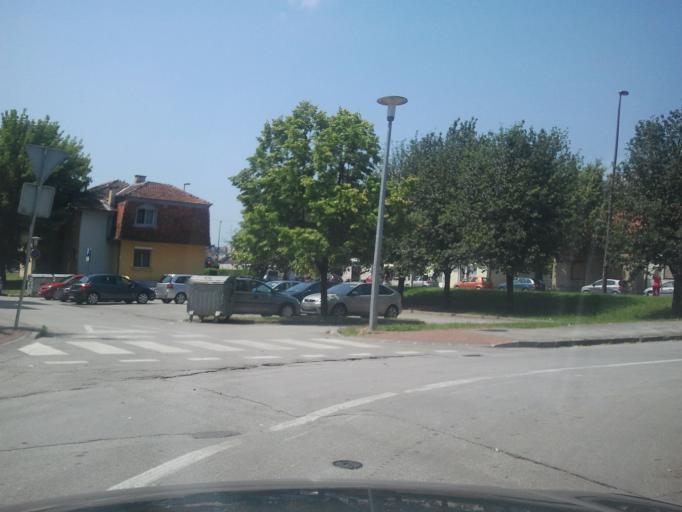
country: HR
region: Karlovacka
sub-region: Grad Karlovac
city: Karlovac
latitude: 45.4841
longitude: 15.5480
